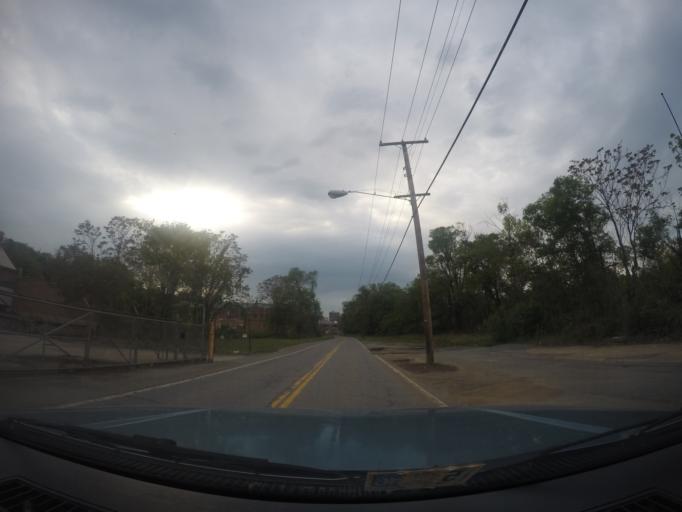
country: US
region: Virginia
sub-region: City of Lynchburg
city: Lynchburg
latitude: 37.4076
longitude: -79.1319
